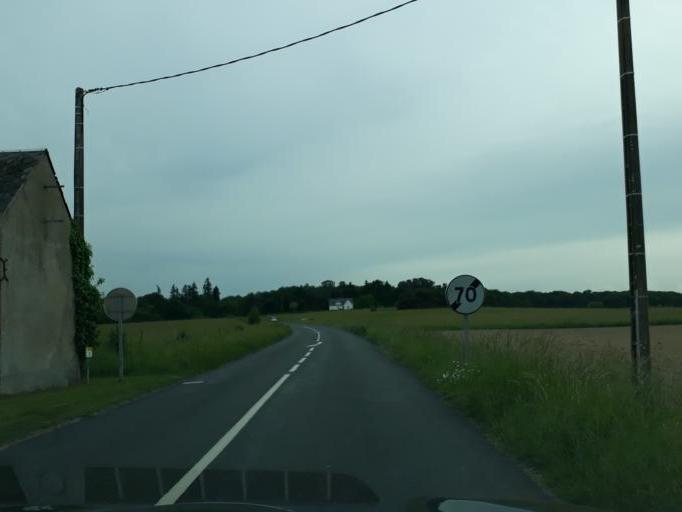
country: FR
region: Centre
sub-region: Departement du Loiret
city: Saint-Pere-sur-Loire
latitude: 47.7512
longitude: 2.3595
